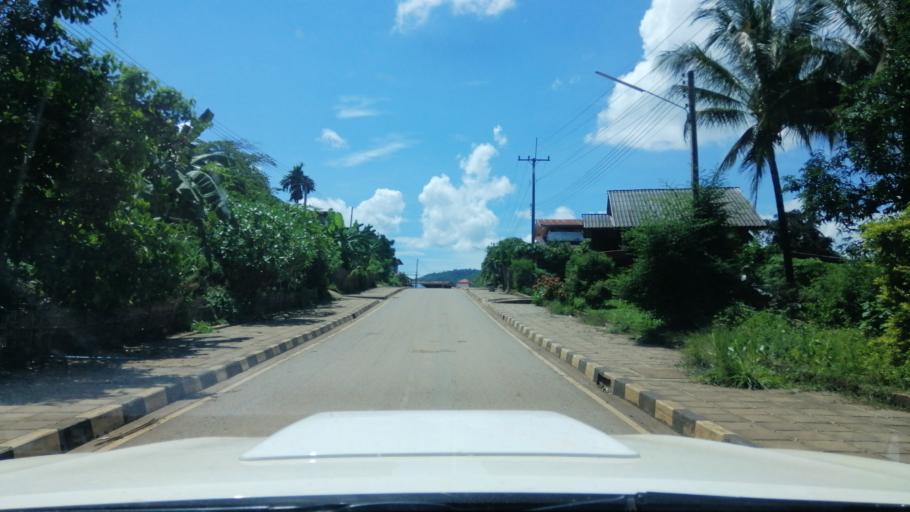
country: TH
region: Uttaradit
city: Ban Khok
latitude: 18.1360
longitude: 101.2716
